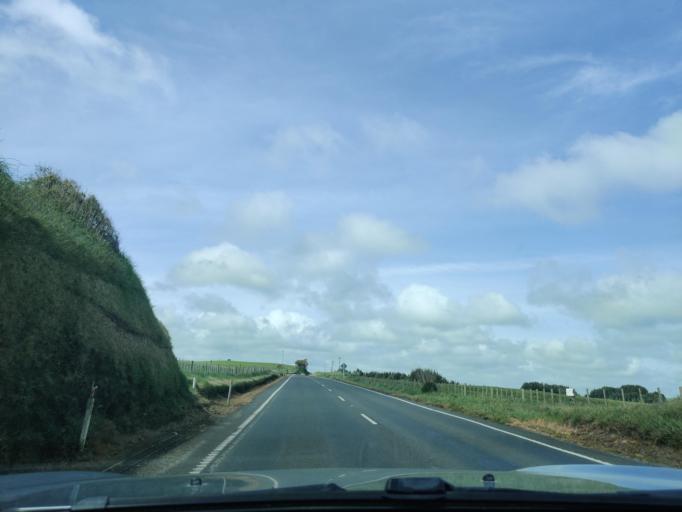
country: NZ
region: Taranaki
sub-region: South Taranaki District
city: Patea
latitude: -39.7673
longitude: 174.5468
